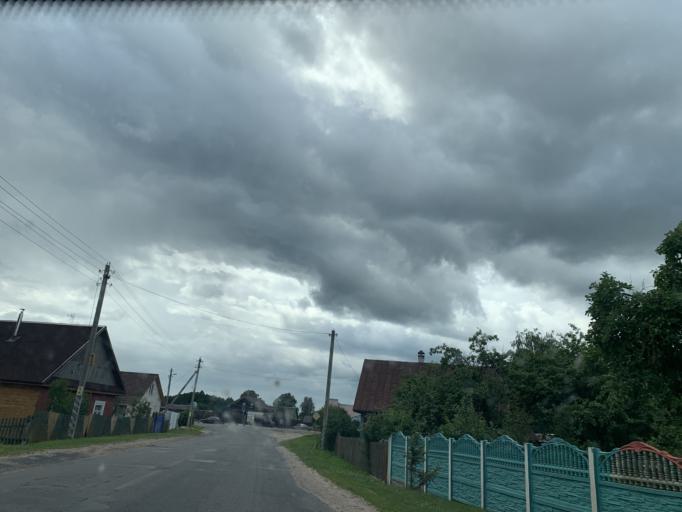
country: BY
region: Minsk
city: Ivyanyets
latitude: 53.9700
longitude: 26.8365
